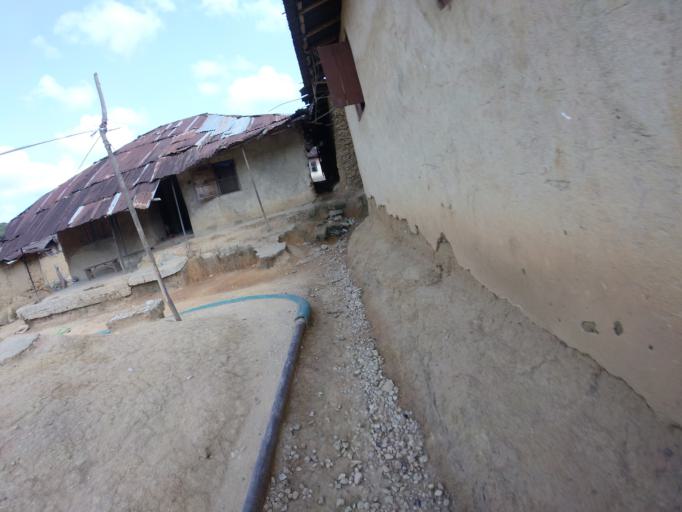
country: SL
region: Eastern Province
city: Jojoima
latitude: 7.6453
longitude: -10.5769
